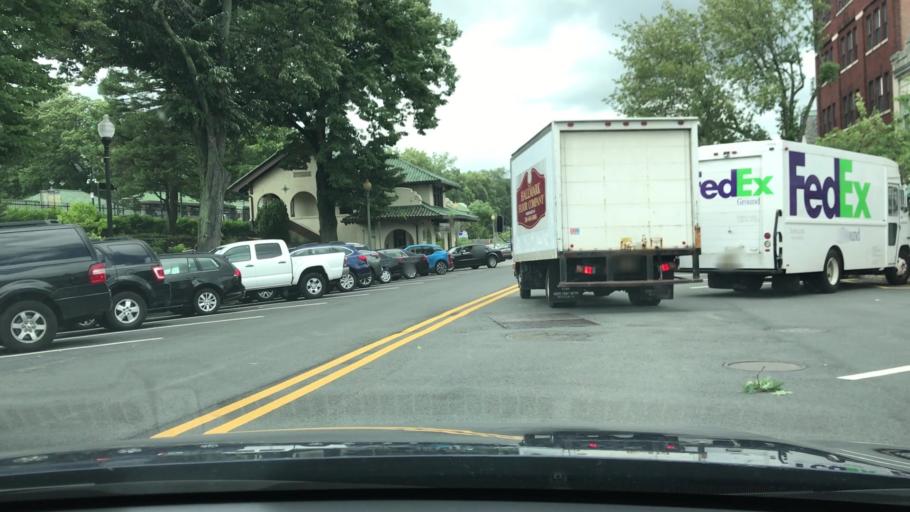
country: US
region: New Jersey
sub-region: Bergen County
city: Ridgewood
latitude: 40.9804
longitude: -74.1203
